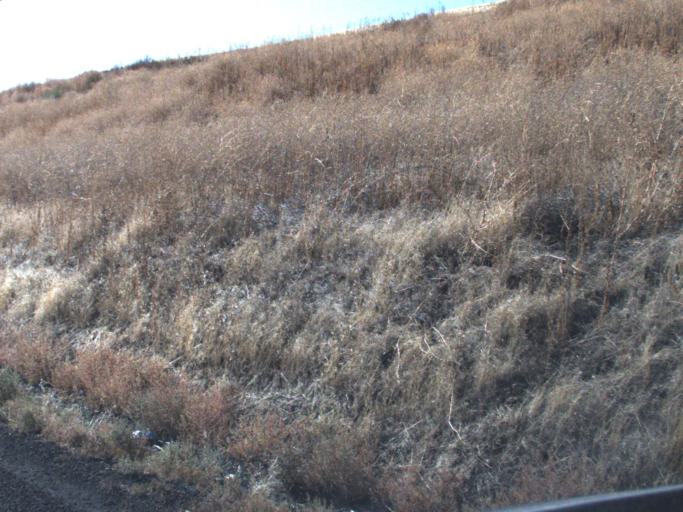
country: US
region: Washington
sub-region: Walla Walla County
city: Waitsburg
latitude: 46.2788
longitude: -118.3454
